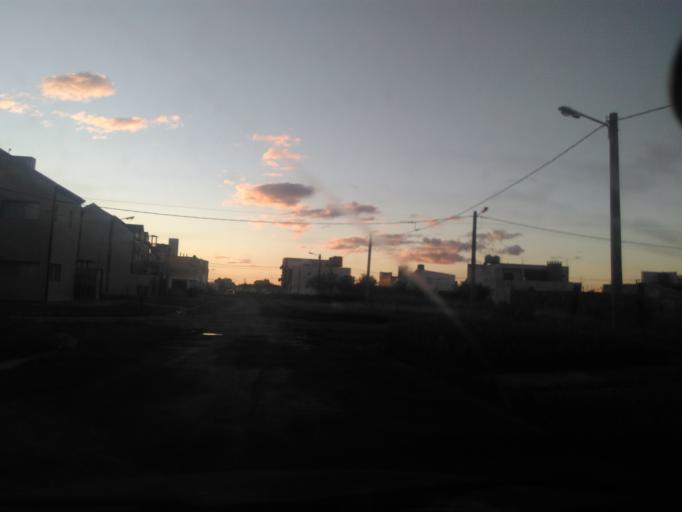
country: AR
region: Chaco
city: Resistencia
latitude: -27.4574
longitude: -59.0100
